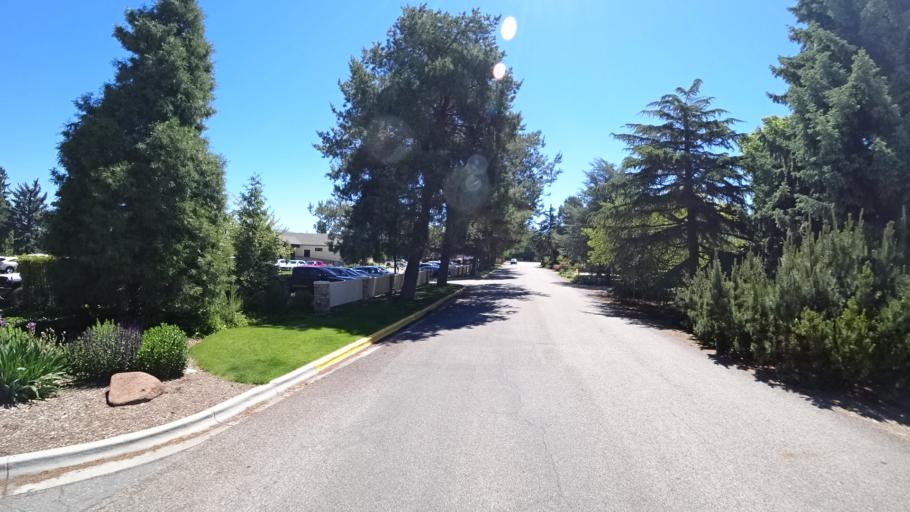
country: US
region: Idaho
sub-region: Ada County
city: Garden City
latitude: 43.5861
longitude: -116.2410
